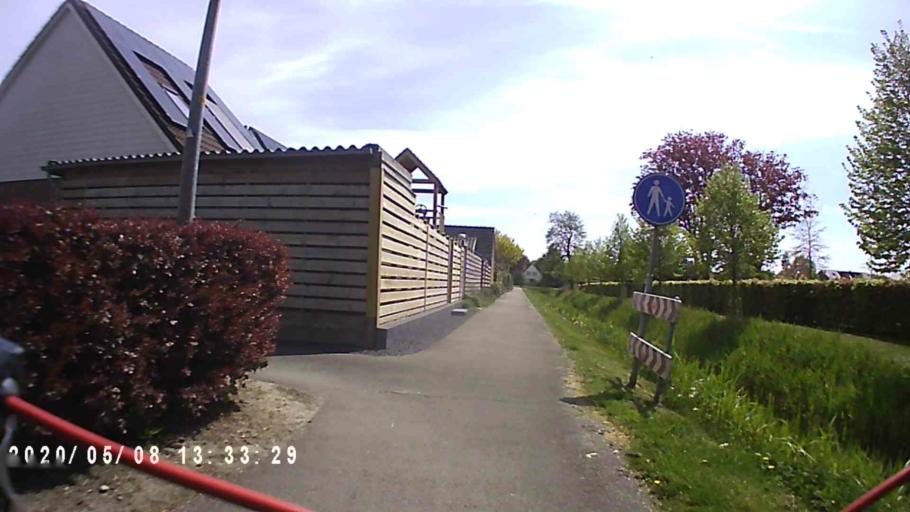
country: NL
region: Groningen
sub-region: Gemeente Appingedam
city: Appingedam
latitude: 53.3303
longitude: 6.7512
